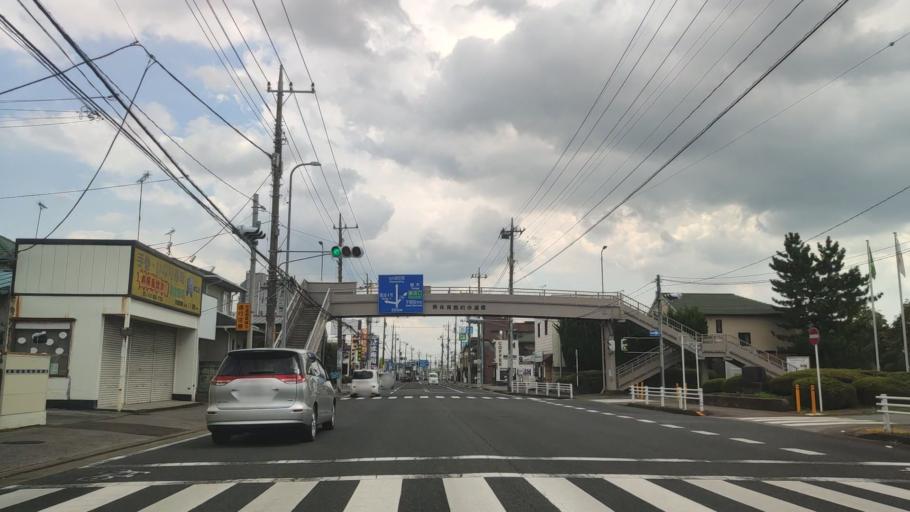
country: JP
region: Tochigi
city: Utsunomiya-shi
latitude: 36.5781
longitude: 139.8702
